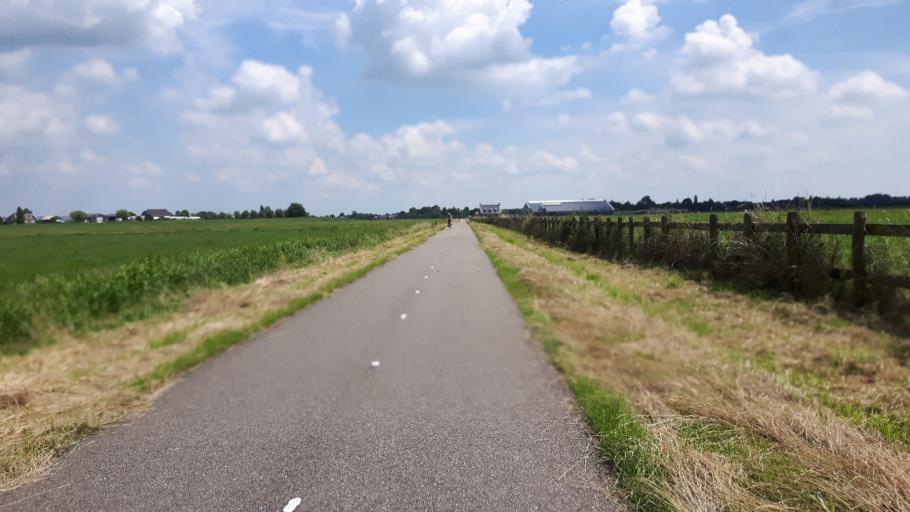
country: NL
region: South Holland
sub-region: Gemeente Boskoop
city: Boskoop
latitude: 52.0746
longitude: 4.6901
